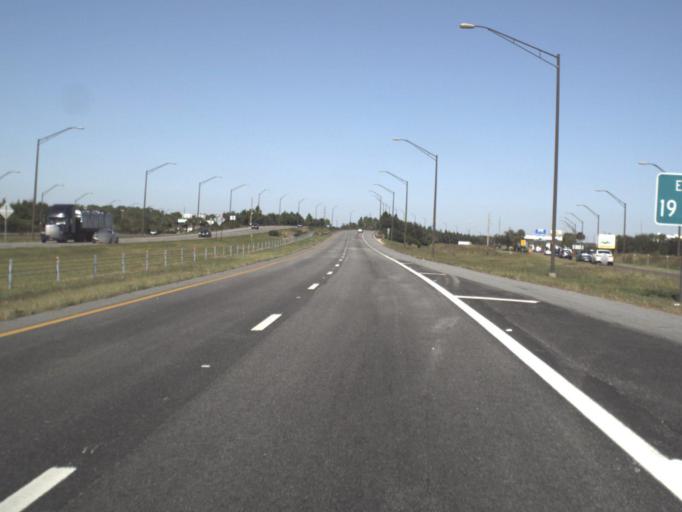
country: US
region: Florida
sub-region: Hillsborough County
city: Cheval
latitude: 28.1850
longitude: -82.5403
